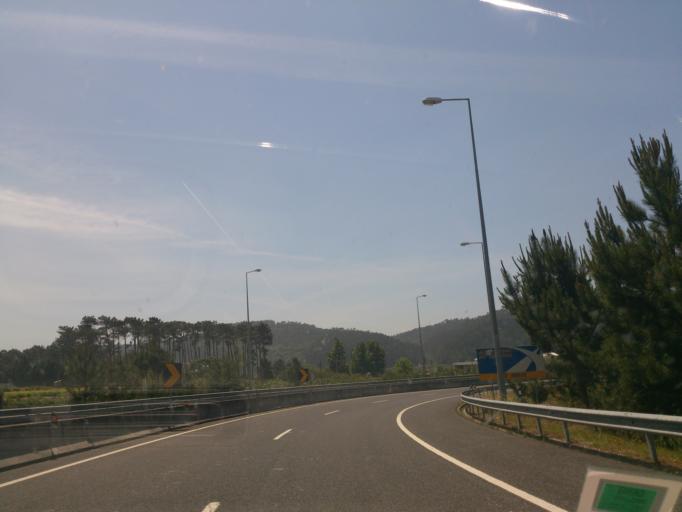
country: PT
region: Leiria
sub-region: Alcobaca
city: Alcobaca
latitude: 39.5832
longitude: -9.0089
